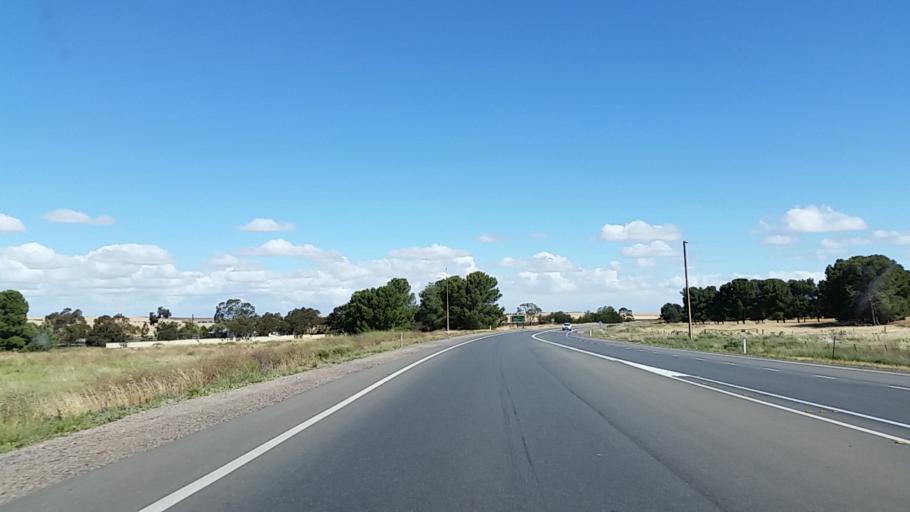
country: AU
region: South Australia
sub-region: Clare and Gilbert Valleys
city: Clare
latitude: -33.7949
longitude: 138.2102
